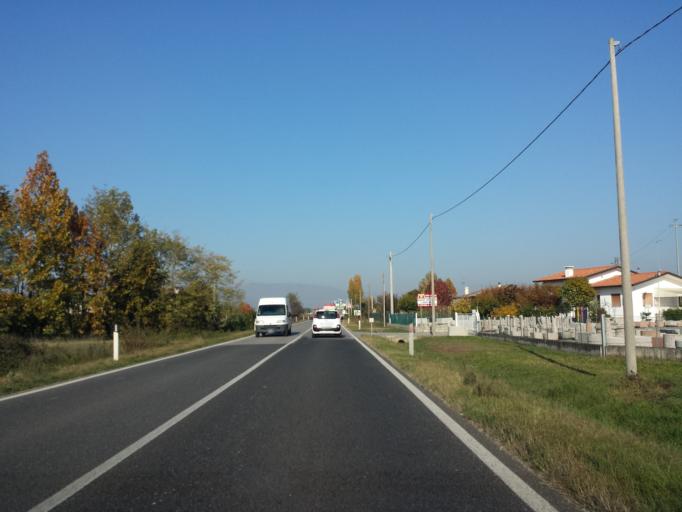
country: IT
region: Veneto
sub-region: Provincia di Treviso
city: Valla
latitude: 45.7204
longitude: 11.9511
